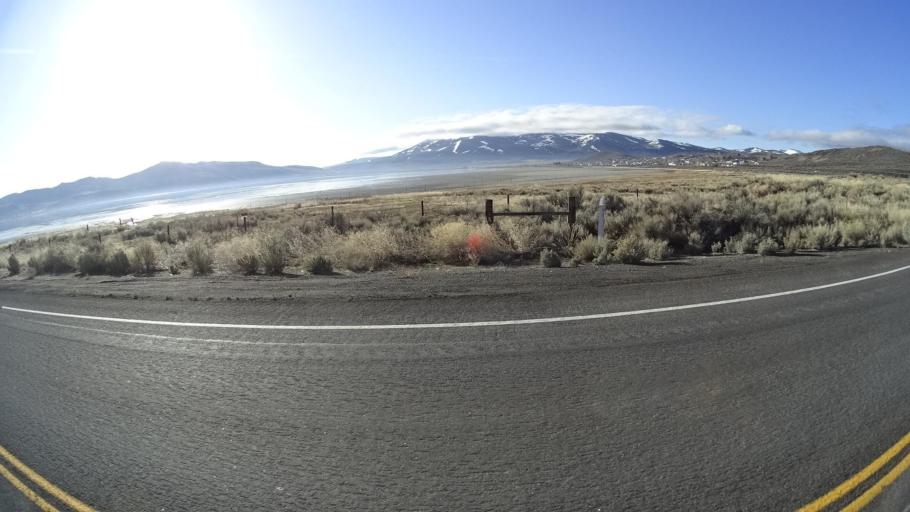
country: US
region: Nevada
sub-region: Washoe County
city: Cold Springs
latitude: 39.6696
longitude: -119.9929
